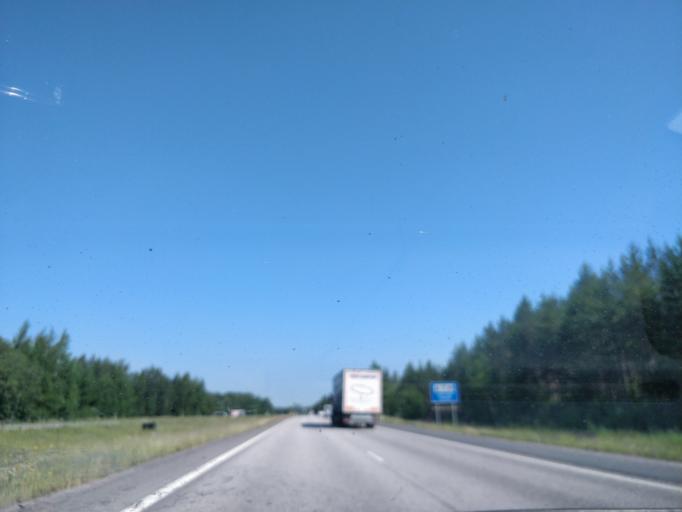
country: FI
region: Haeme
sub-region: Riihimaeki
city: Riihimaeki
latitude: 60.7068
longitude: 24.7378
